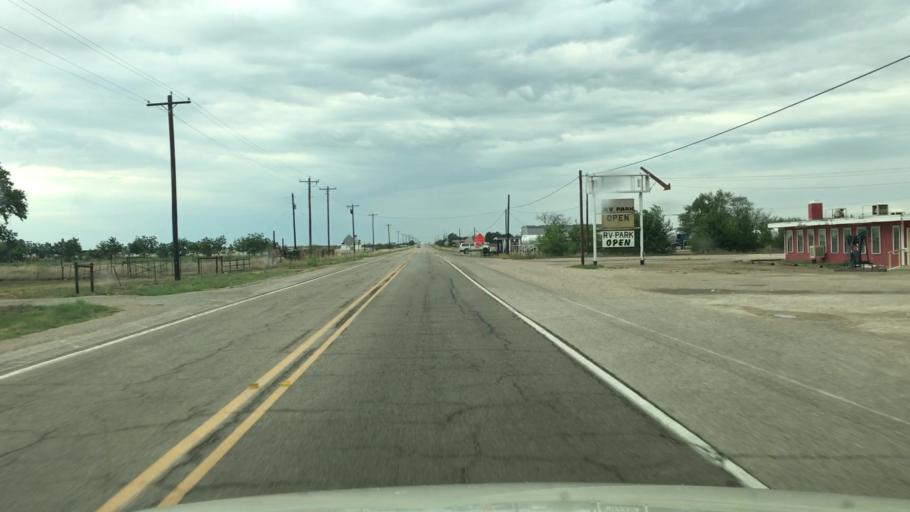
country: US
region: New Mexico
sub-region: Lea County
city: Lovington
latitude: 33.2570
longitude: -103.3394
